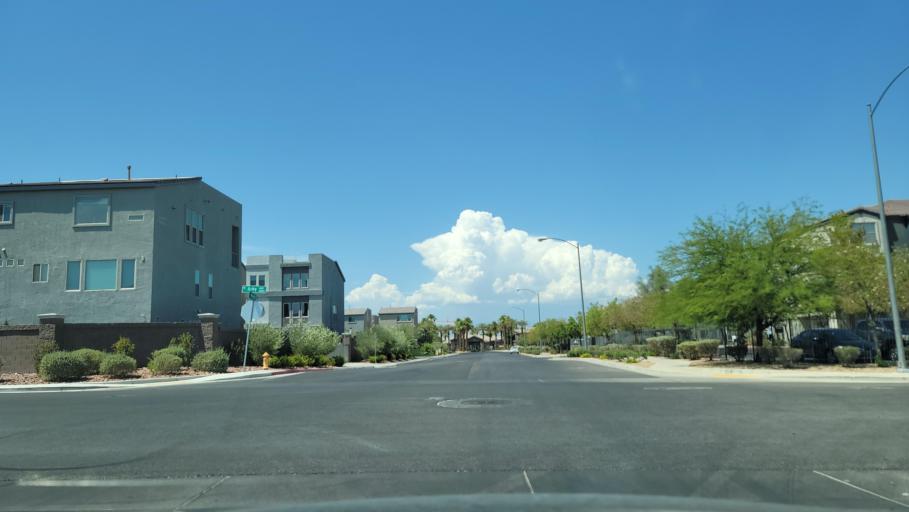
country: US
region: Nevada
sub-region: Clark County
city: Enterprise
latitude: 36.0591
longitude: -115.2655
